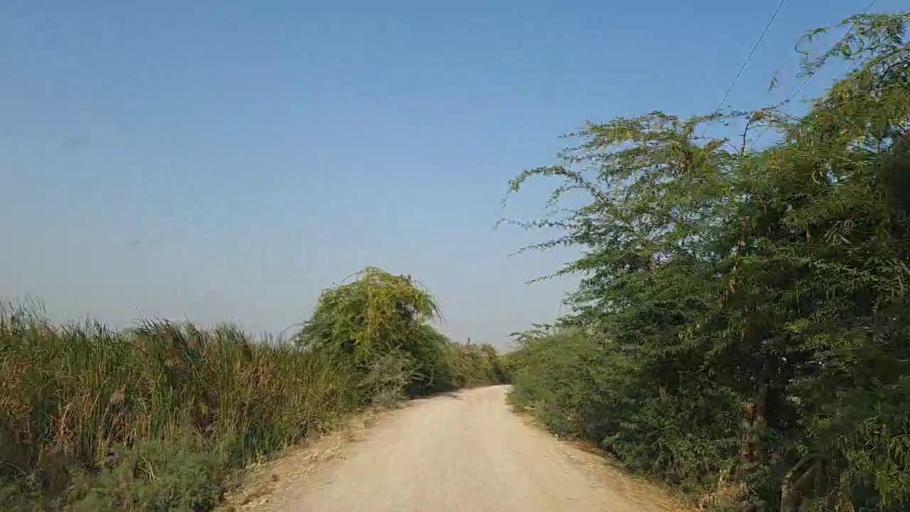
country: PK
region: Sindh
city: Jati
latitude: 24.5221
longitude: 68.2634
